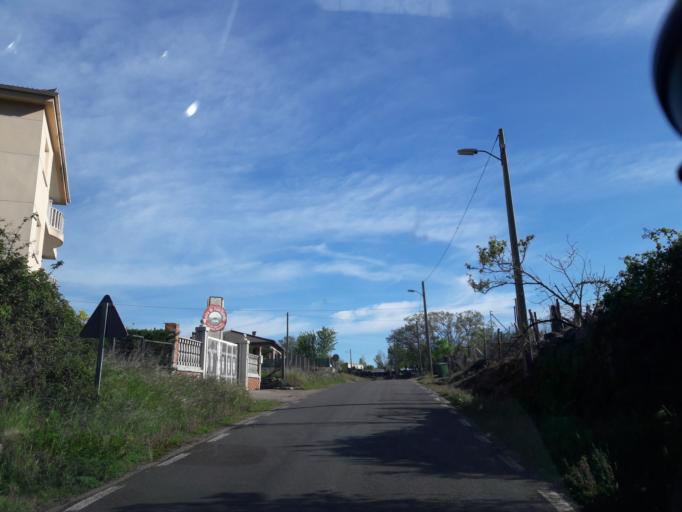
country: ES
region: Castille and Leon
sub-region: Provincia de Salamanca
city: Sanchotello
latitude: 40.4355
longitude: -5.7523
